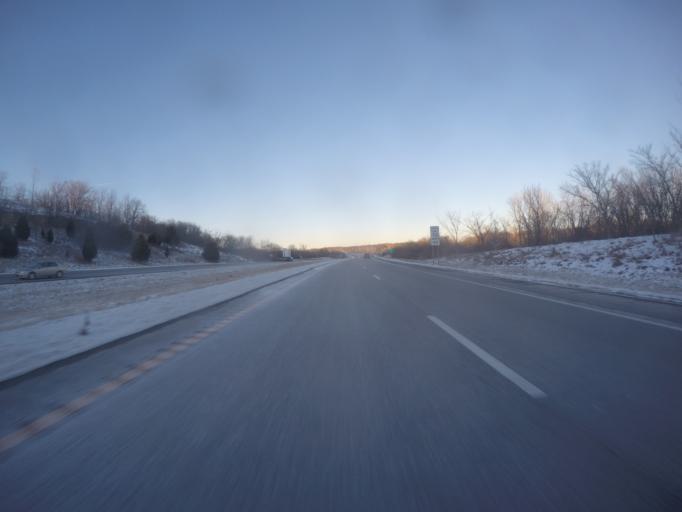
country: US
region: Missouri
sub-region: Platte County
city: Weatherby Lake
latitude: 39.2333
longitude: -94.7588
